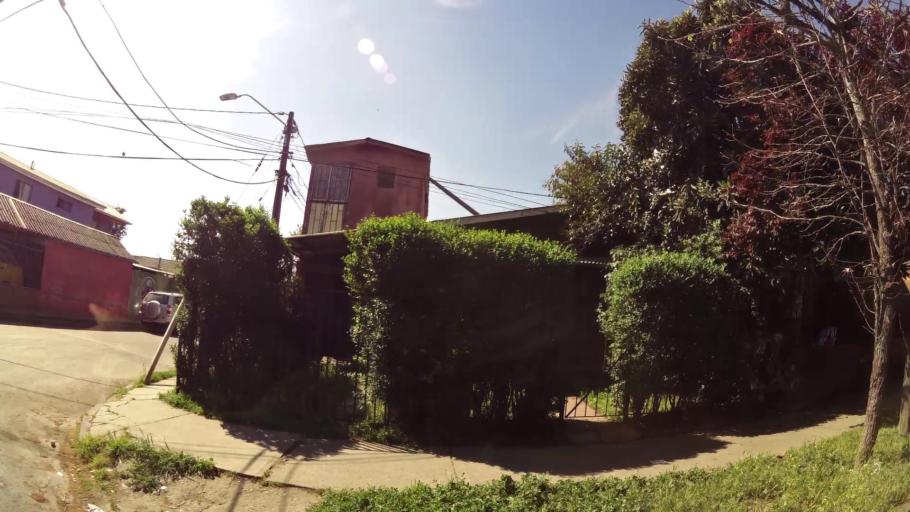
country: CL
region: Santiago Metropolitan
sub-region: Provincia de Santiago
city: Villa Presidente Frei, Nunoa, Santiago, Chile
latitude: -33.4990
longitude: -70.5789
